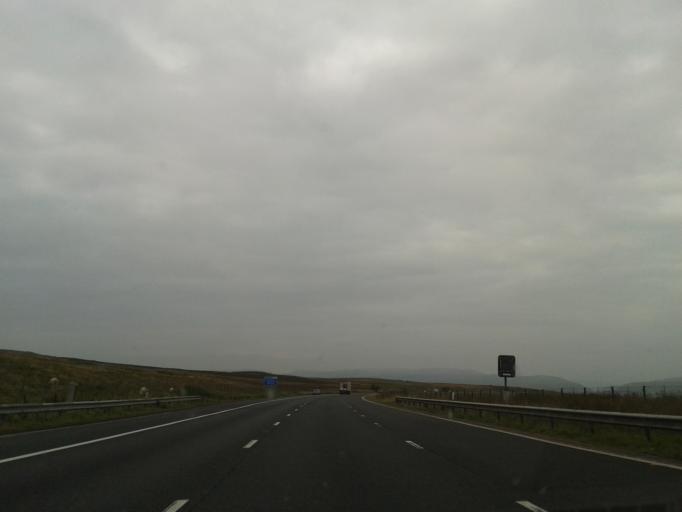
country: GB
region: England
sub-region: Cumbria
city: Appleby-in-Westmorland
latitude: 54.4877
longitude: -2.6375
